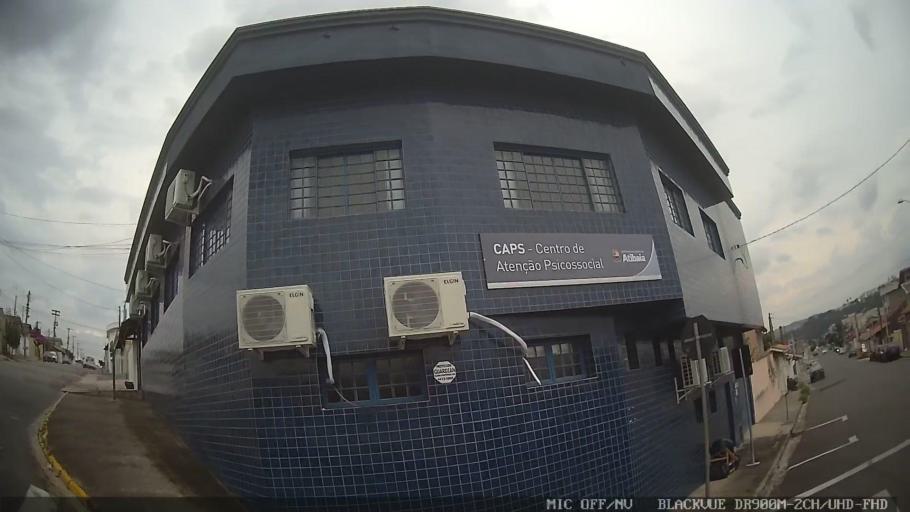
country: BR
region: Sao Paulo
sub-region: Atibaia
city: Atibaia
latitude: -23.1293
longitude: -46.5579
